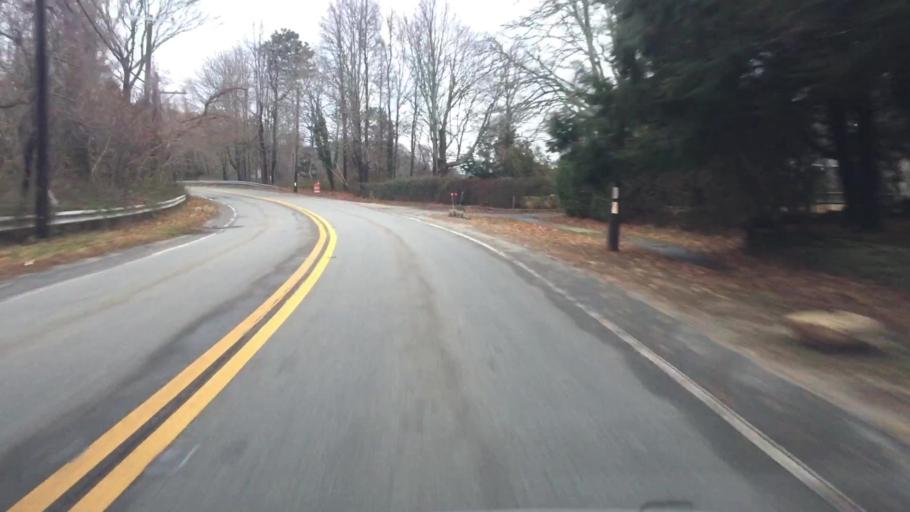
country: US
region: Massachusetts
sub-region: Barnstable County
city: West Falmouth
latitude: 41.5978
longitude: -70.6369
